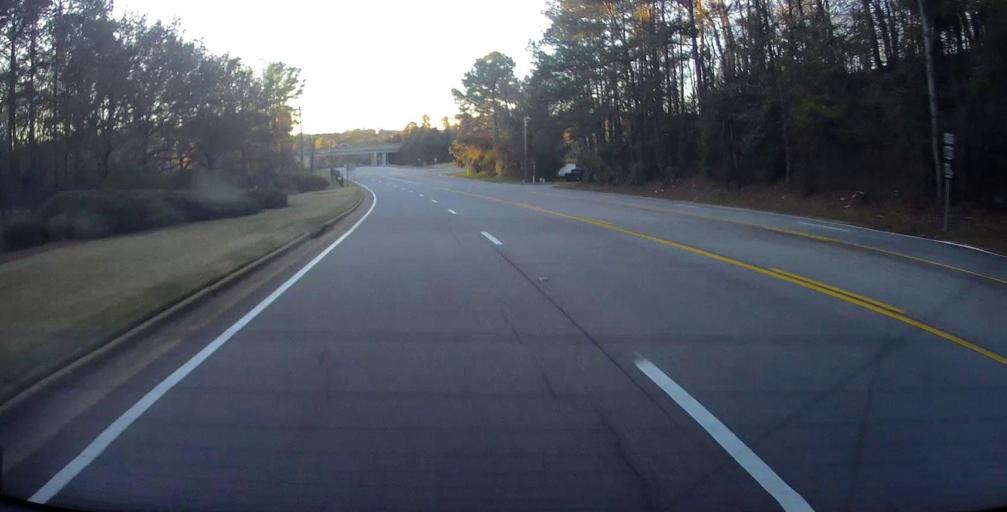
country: US
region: Alabama
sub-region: Russell County
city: Phenix City
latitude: 32.5193
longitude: -84.9874
